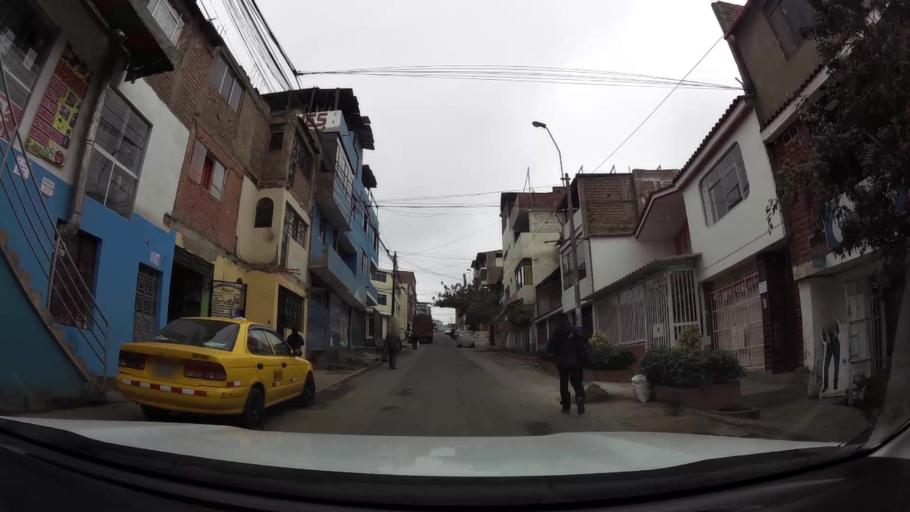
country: PE
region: Lima
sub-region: Lima
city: Surco
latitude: -12.1650
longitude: -76.9547
